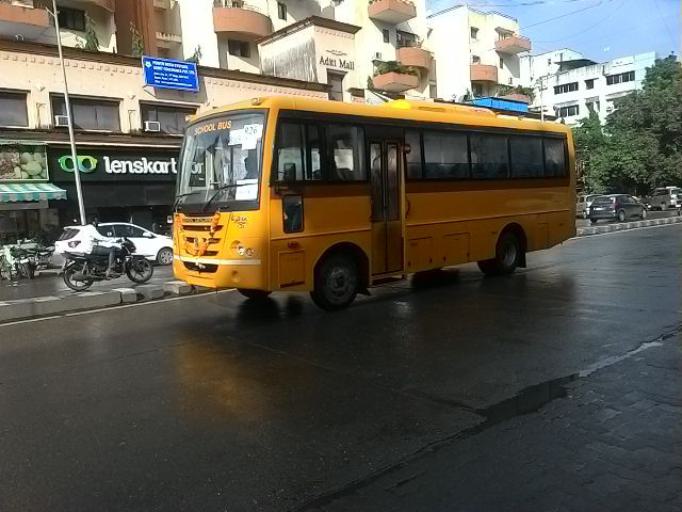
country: IN
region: Maharashtra
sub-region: Pune Division
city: Khadki
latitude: 18.5582
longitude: 73.7923
